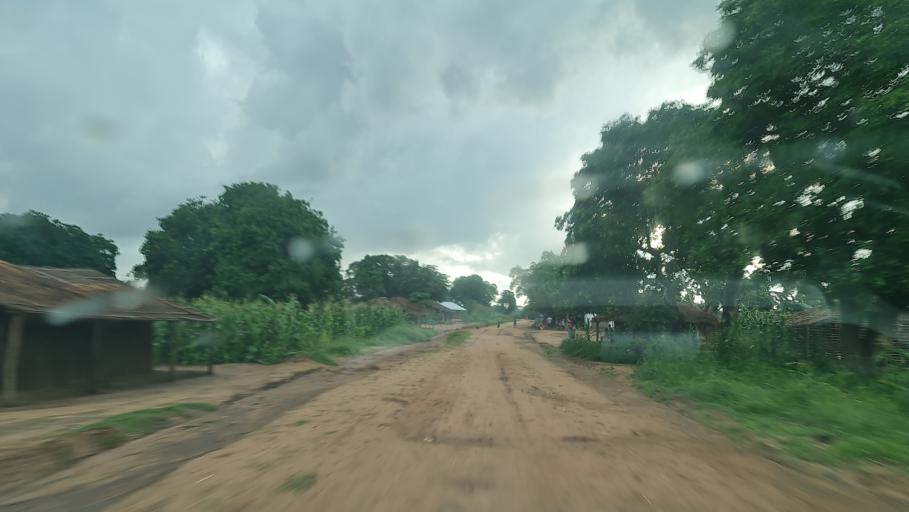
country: MZ
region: Nampula
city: Nacala
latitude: -13.9899
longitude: 40.3731
